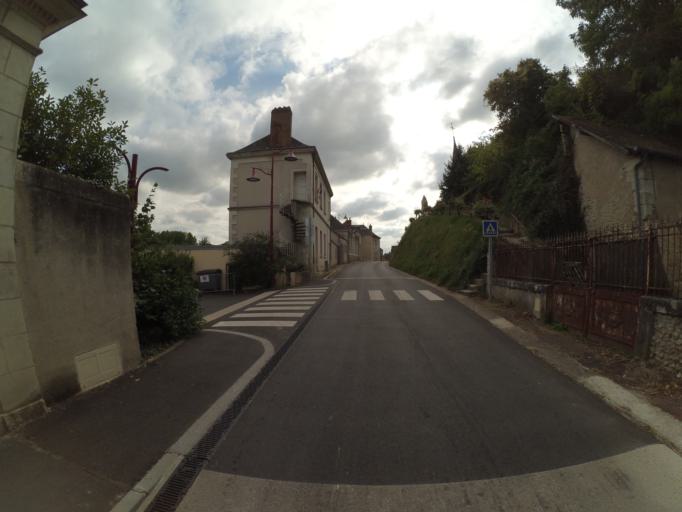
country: FR
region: Centre
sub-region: Departement d'Indre-et-Loire
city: Reugny
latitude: 47.4534
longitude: 0.8742
